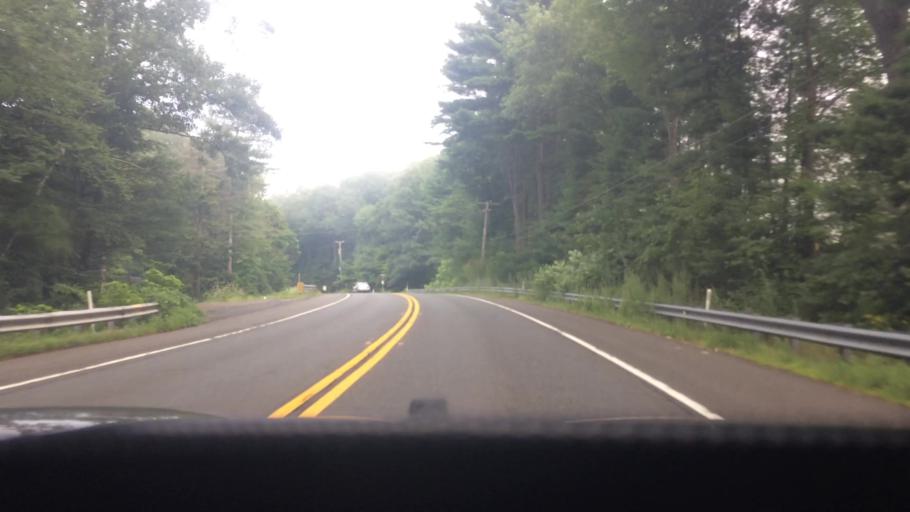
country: US
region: Massachusetts
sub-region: Franklin County
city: Millers Falls
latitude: 42.6080
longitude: -72.5059
